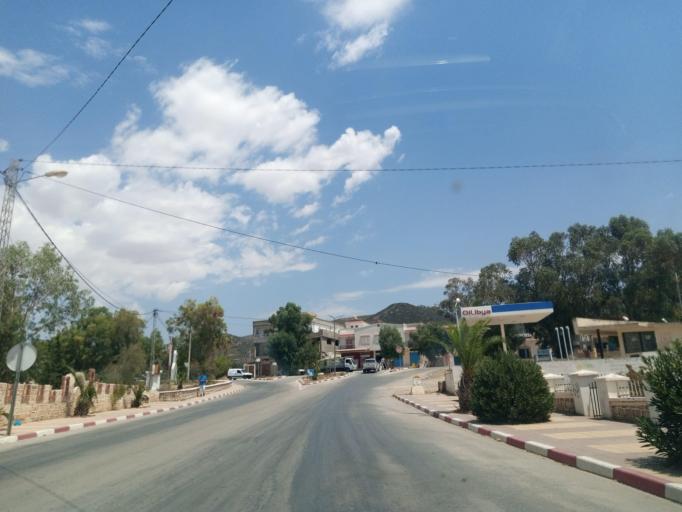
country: TN
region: Kef
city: Nibbar
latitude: 36.3078
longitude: 8.7738
